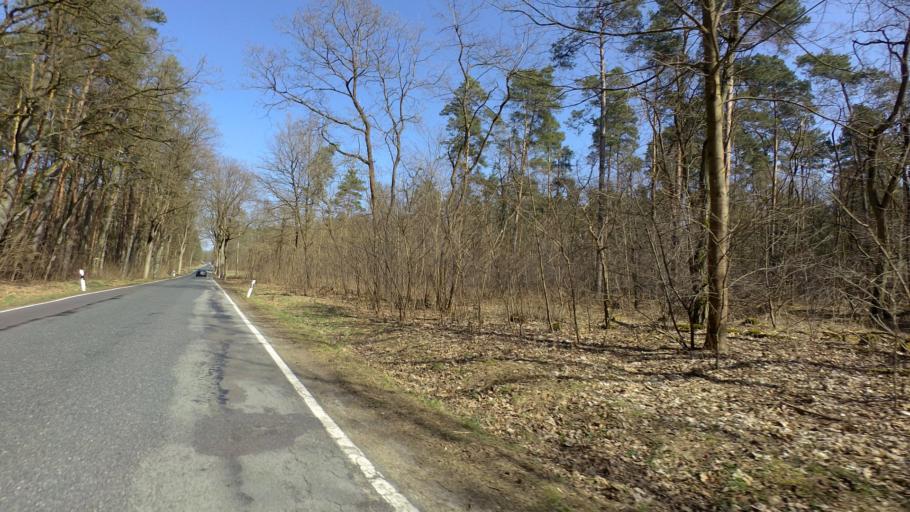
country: DE
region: Brandenburg
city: Ruthnick
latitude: 52.9197
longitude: 12.9615
